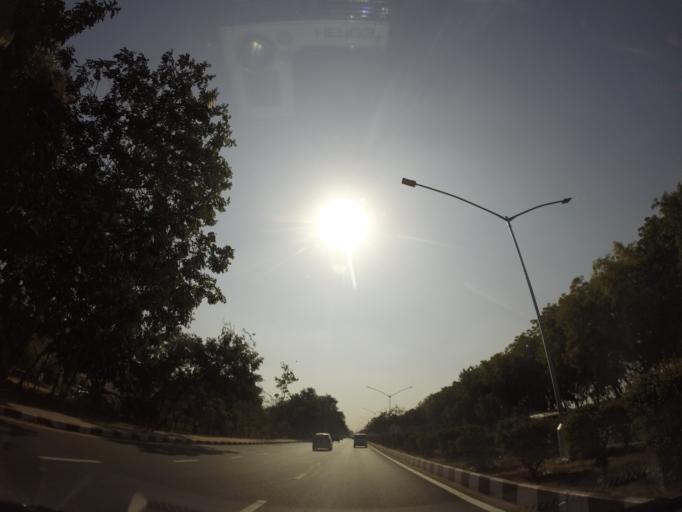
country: IN
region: Gujarat
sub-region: Gandhinagar
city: Ghandinagar
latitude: 23.2143
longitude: 72.6396
